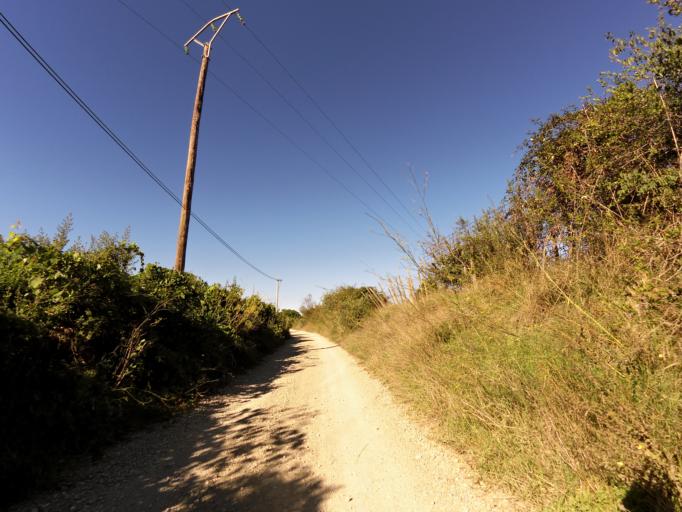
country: FR
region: Languedoc-Roussillon
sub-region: Departement du Gard
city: Gallargues-le-Montueux
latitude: 43.7257
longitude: 4.1541
